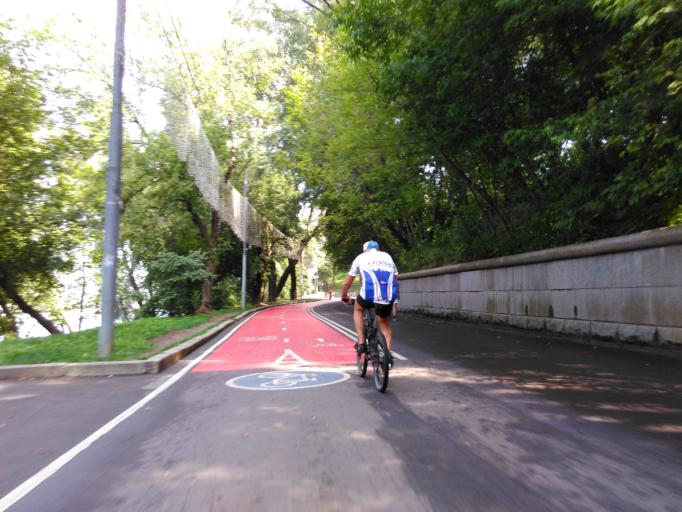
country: RU
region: Moscow
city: Novyye Cheremushki
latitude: 55.7181
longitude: 37.5858
